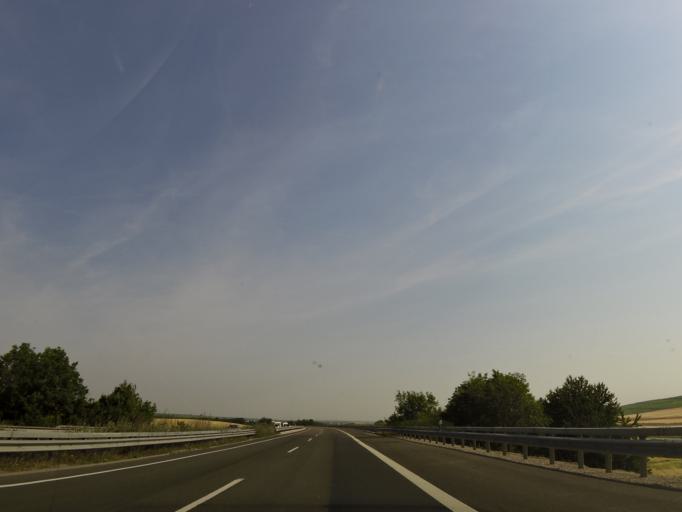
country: DE
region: Rheinland-Pfalz
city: Dintesheim
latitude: 49.7279
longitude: 8.1365
